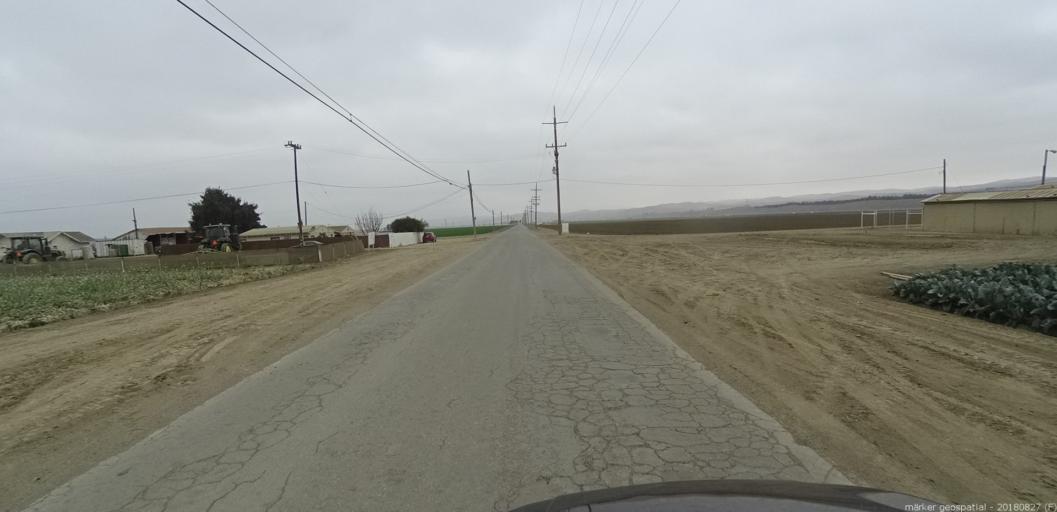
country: US
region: California
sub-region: Monterey County
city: King City
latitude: 36.2491
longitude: -121.1489
